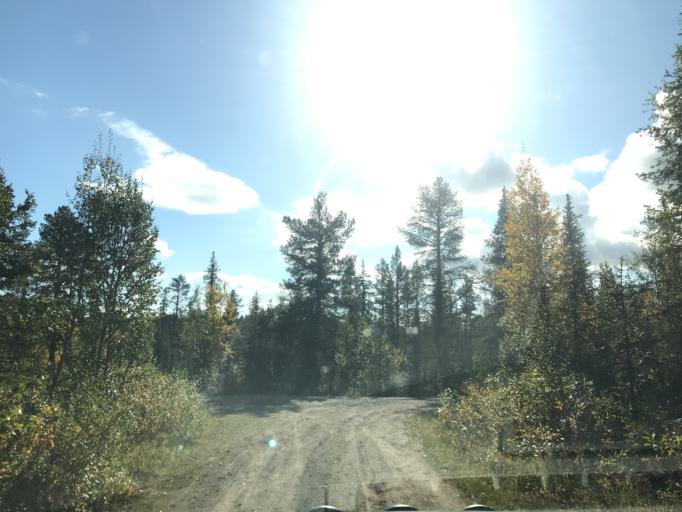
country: SE
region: Norrbotten
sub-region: Gallivare Kommun
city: Malmberget
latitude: 67.6475
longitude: 21.0843
